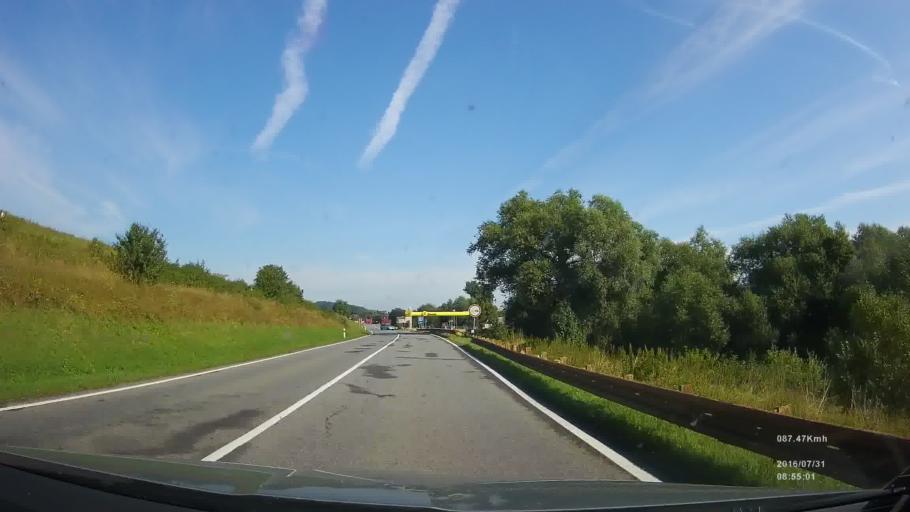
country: SK
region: Presovsky
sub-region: Okres Bardejov
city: Bardejov
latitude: 49.1417
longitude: 21.3237
